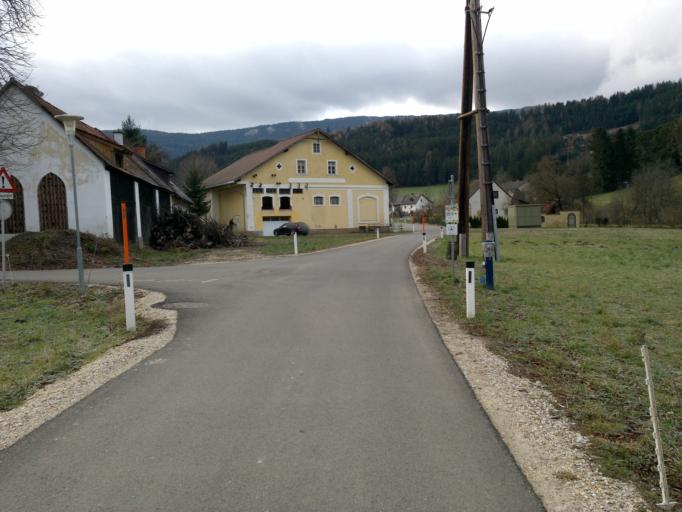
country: AT
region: Styria
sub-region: Politischer Bezirk Murtal
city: Obdach
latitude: 47.0760
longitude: 14.6848
